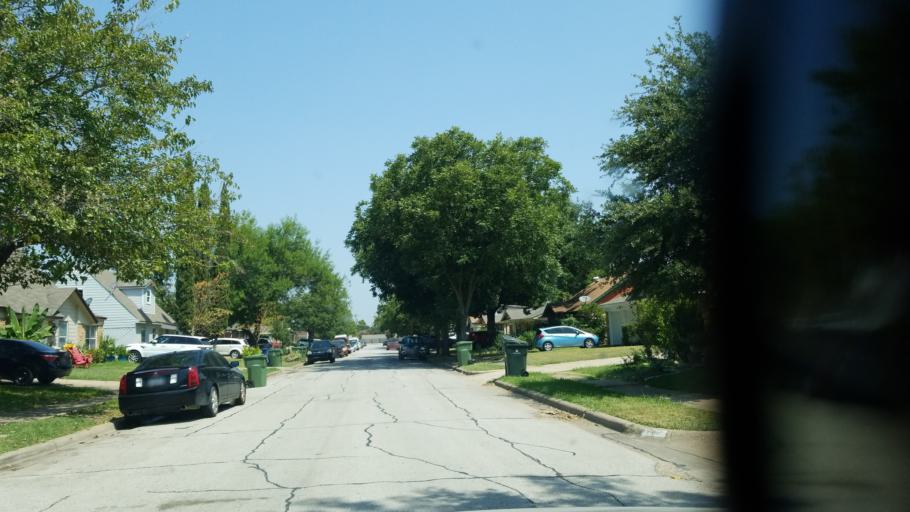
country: US
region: Texas
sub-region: Dallas County
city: Garland
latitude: 32.9197
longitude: -96.6237
